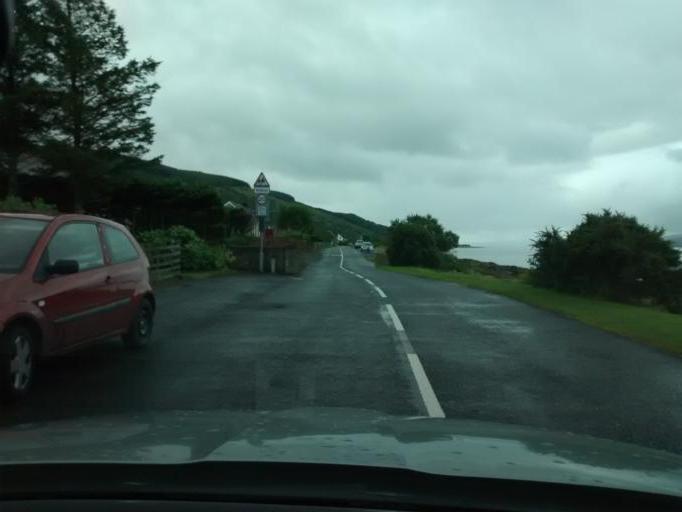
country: GB
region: Scotland
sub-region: North Ayrshire
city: Isle of Arran
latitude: 55.6482
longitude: -5.3816
